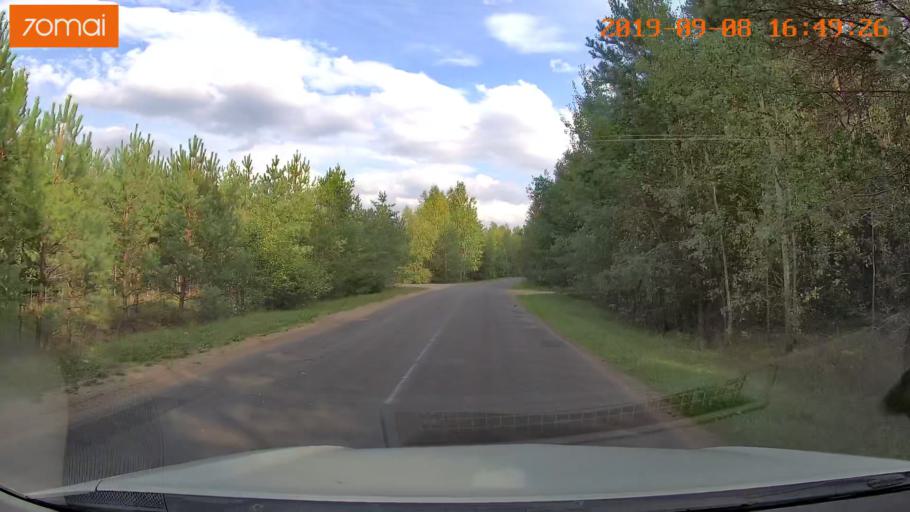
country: BY
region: Grodnenskaya
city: Hrodna
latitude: 53.8099
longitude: 23.8738
